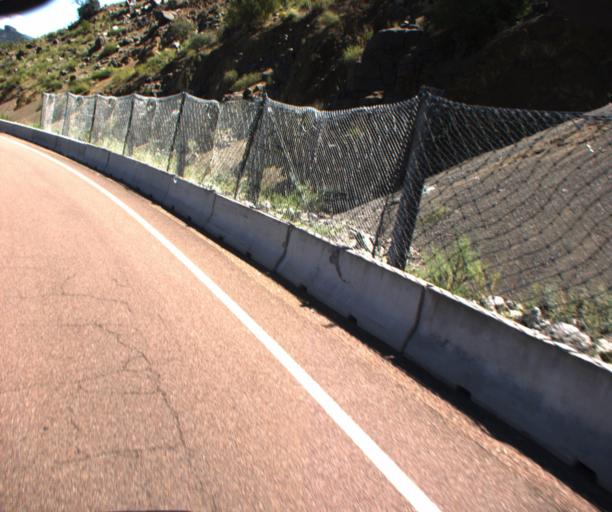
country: US
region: Arizona
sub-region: Navajo County
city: Cibecue
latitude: 33.7914
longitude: -110.4999
